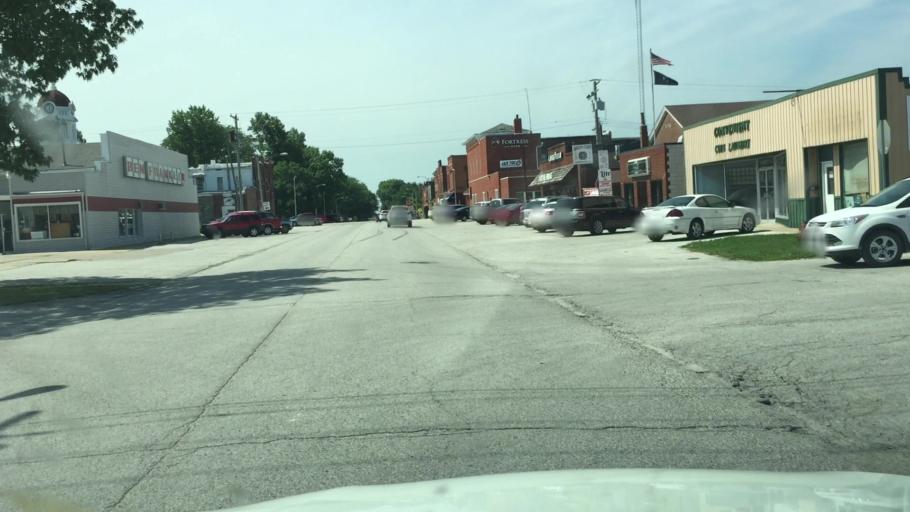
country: US
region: Illinois
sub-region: Hancock County
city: Carthage
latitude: 40.4151
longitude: -91.1363
